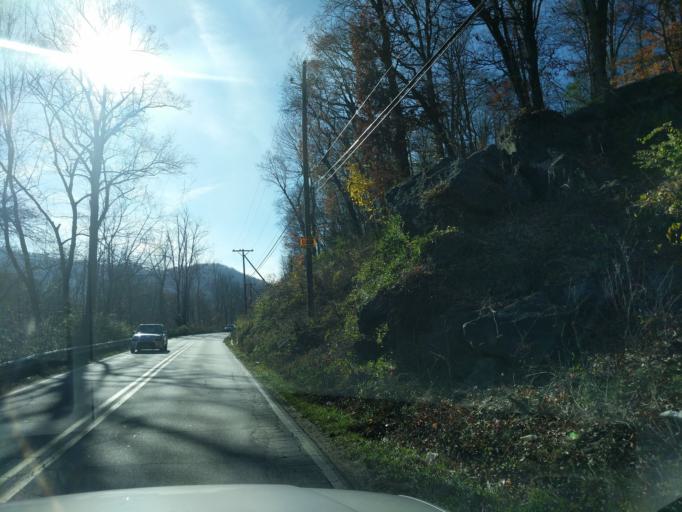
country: US
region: North Carolina
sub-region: Buncombe County
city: Swannanoa
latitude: 35.6042
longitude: -82.3942
